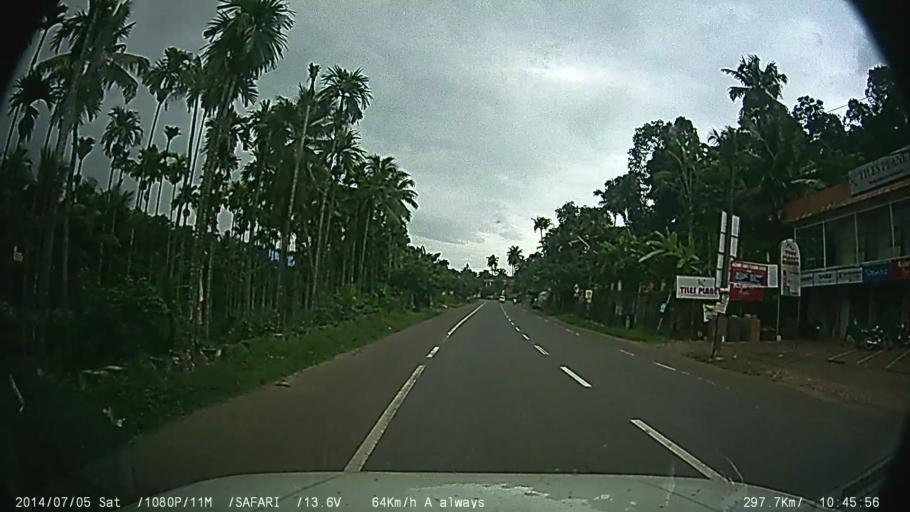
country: IN
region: Kerala
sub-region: Ernakulam
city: Muvattupula
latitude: 9.9757
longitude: 76.5936
